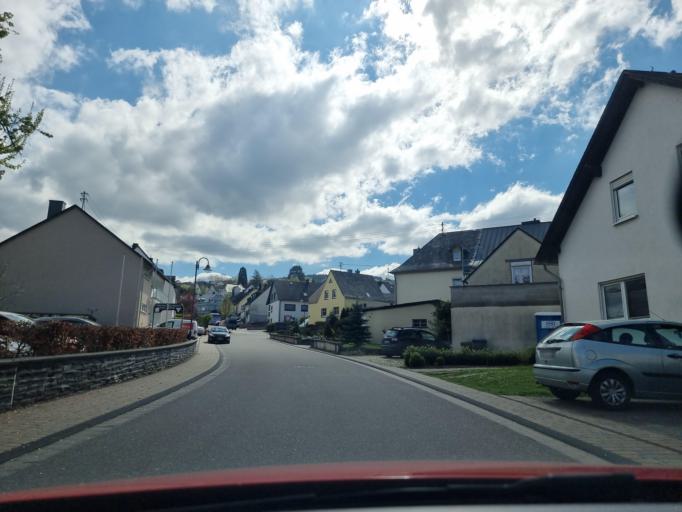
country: DE
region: Rheinland-Pfalz
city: Mertesdorf
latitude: 49.7739
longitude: 6.7238
